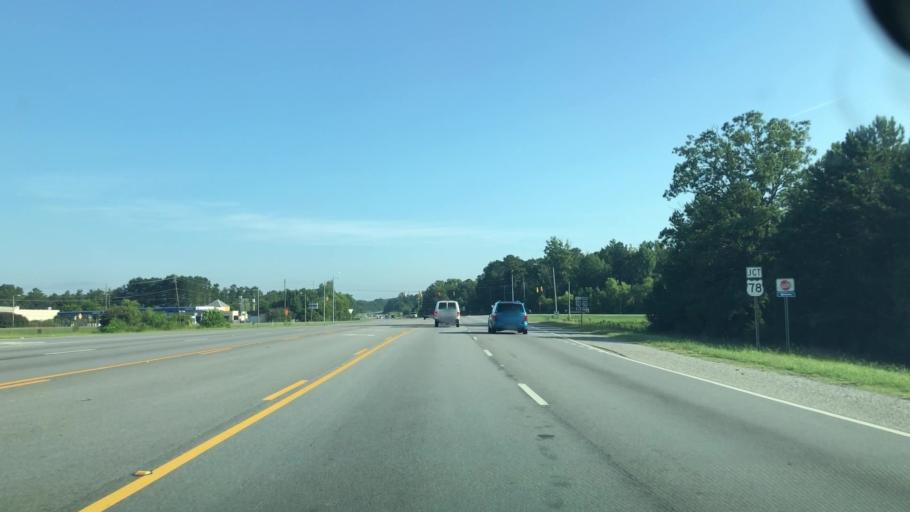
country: US
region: Alabama
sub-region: Calhoun County
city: Bynum
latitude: 33.5945
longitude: -85.9249
